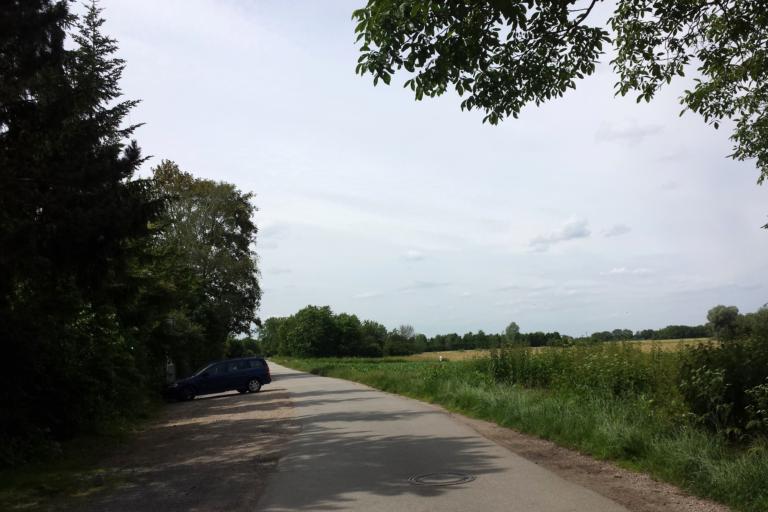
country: DE
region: Baden-Wuerttemberg
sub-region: Karlsruhe Region
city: Dossenheim
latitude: 49.4361
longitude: 8.6508
